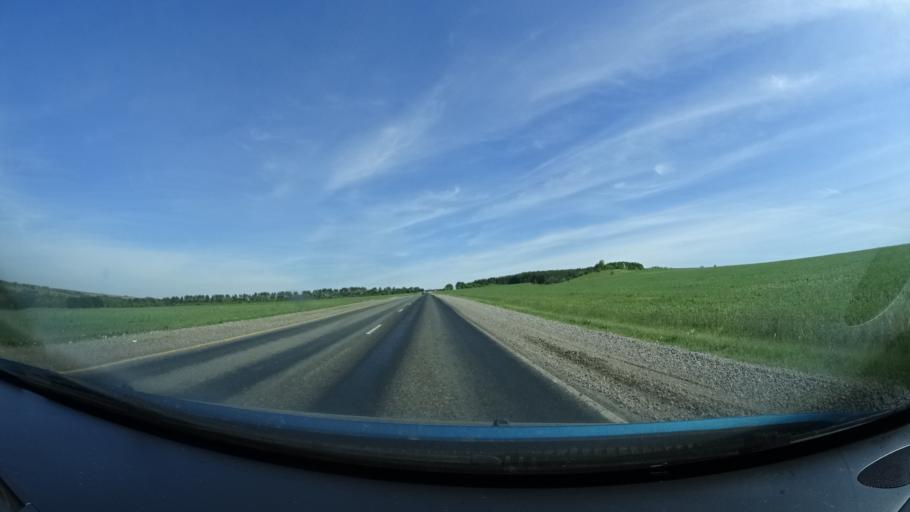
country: RU
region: Bashkortostan
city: Blagoveshchensk
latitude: 55.1269
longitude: 55.8427
